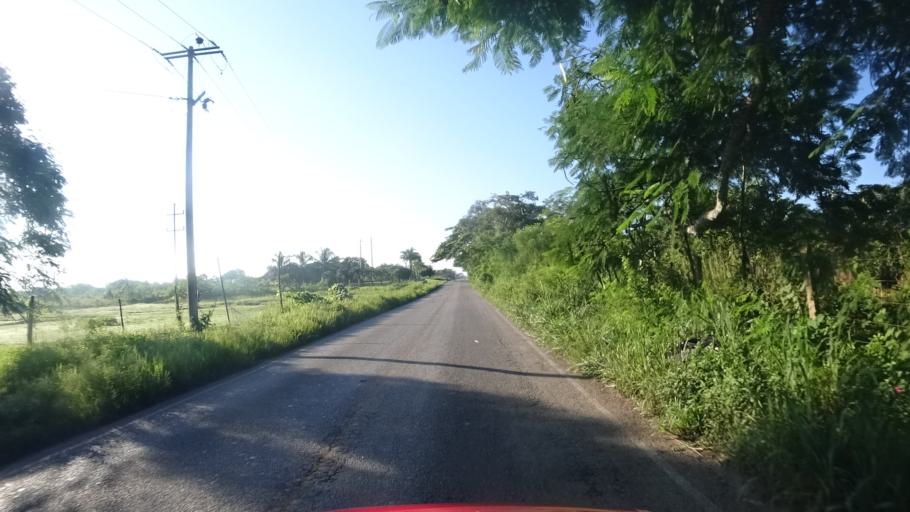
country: MX
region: Yucatan
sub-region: Tizimin
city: Tizimin
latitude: 21.1897
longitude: -88.1674
